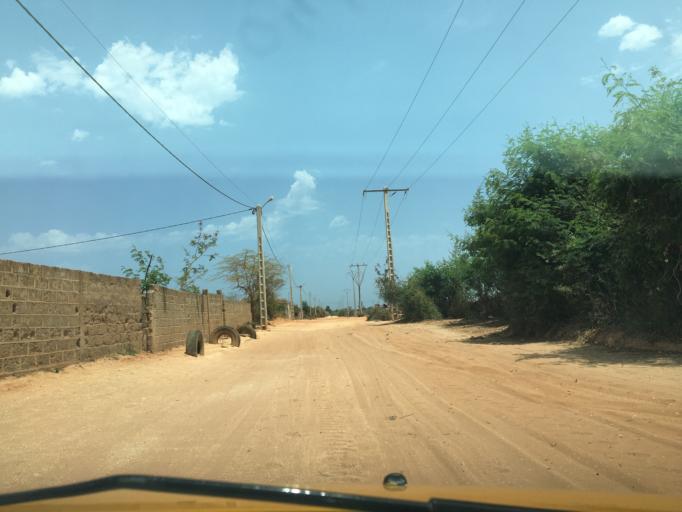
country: SN
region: Thies
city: Thies
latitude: 14.8101
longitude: -17.1905
